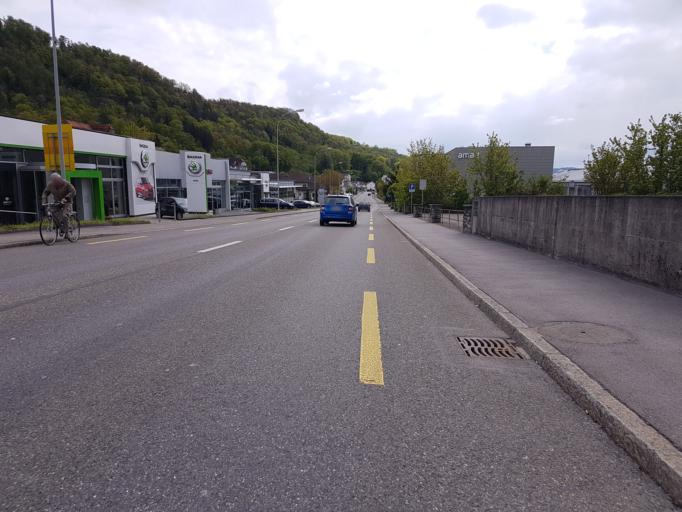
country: CH
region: Aargau
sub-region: Bezirk Brugg
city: Schinznach Bad
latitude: 47.4489
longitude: 8.1685
